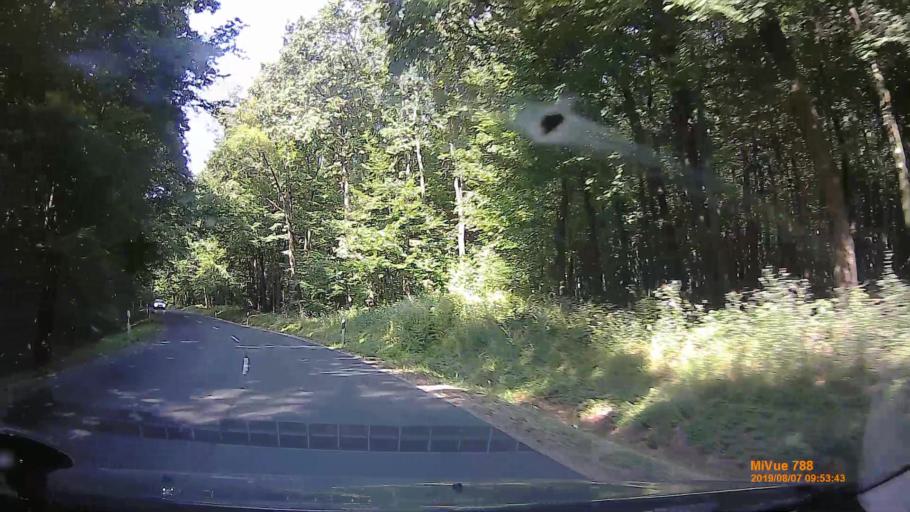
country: HU
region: Zala
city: Zalaegerszeg
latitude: 46.7353
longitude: 16.8796
